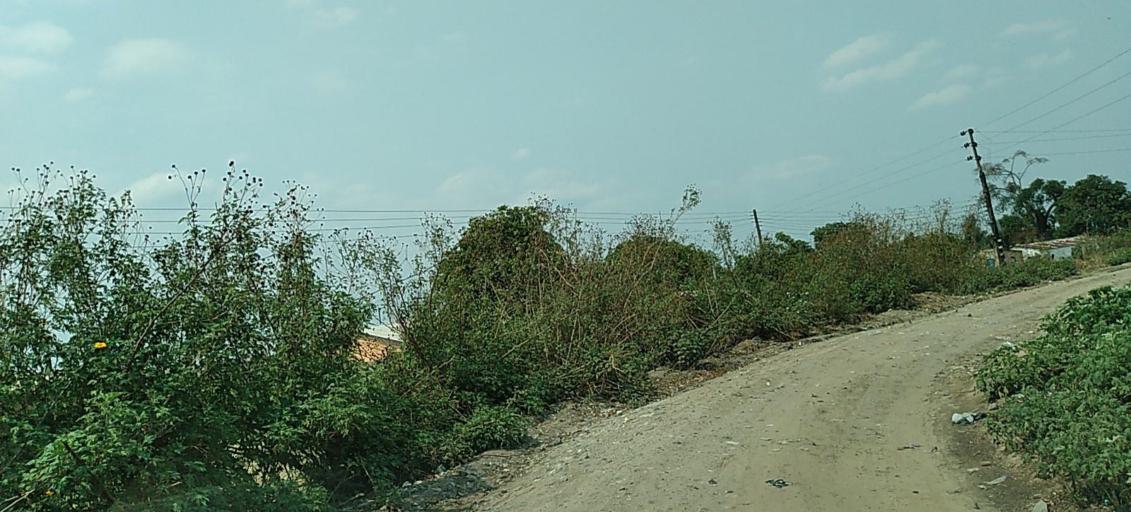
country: ZM
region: Copperbelt
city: Chambishi
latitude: -12.6310
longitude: 28.0744
